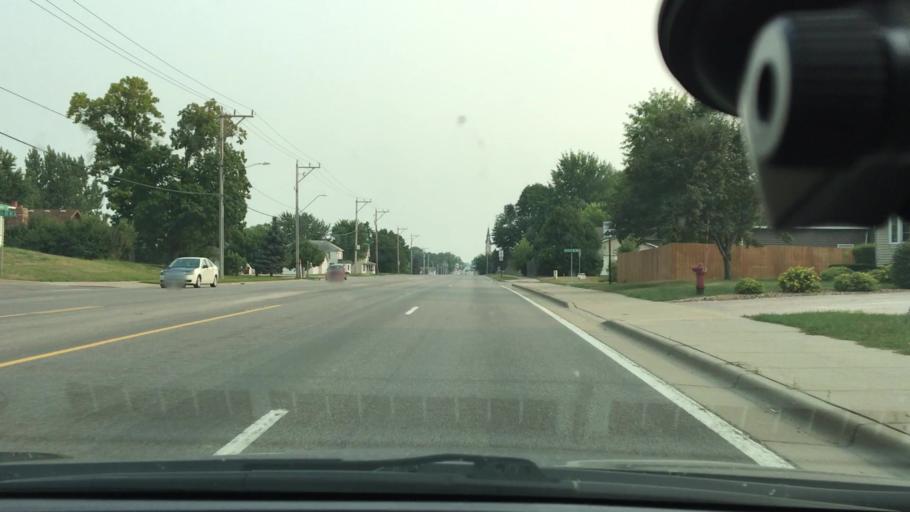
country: US
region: Minnesota
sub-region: Wright County
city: Saint Michael
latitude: 45.2190
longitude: -93.6647
